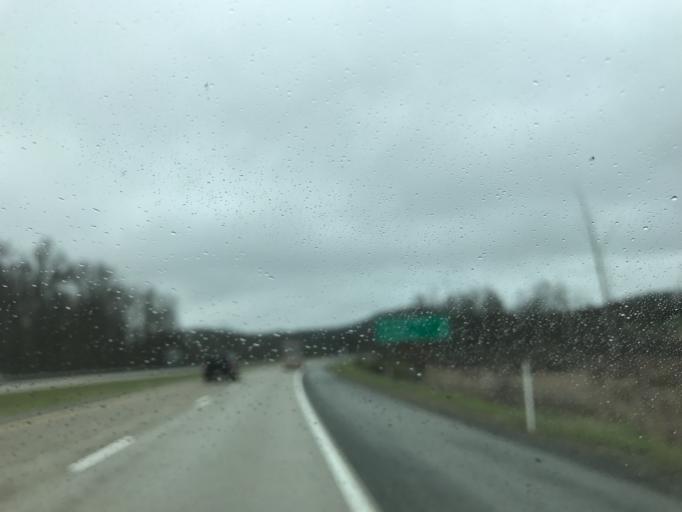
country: US
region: West Virginia
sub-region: Greenbrier County
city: Rainelle
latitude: 37.8611
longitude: -80.7145
